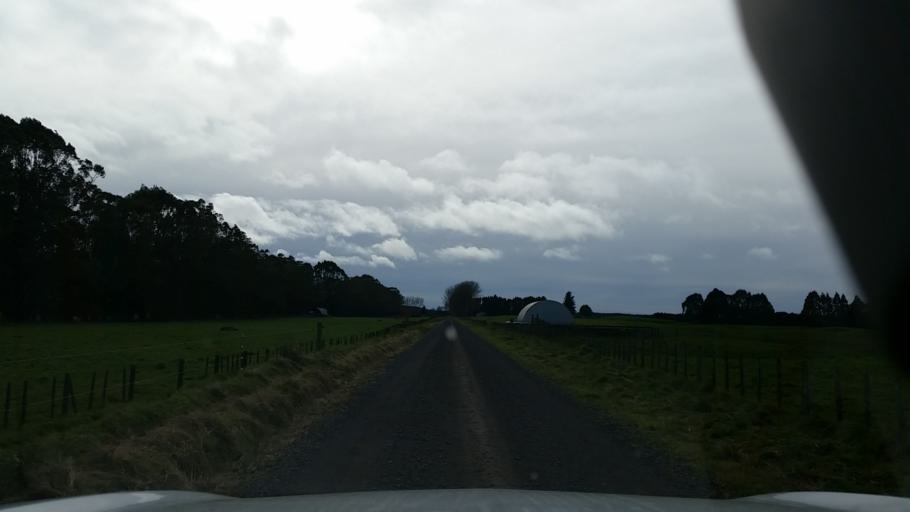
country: NZ
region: Bay of Plenty
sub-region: Whakatane District
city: Murupara
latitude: -38.4789
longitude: 176.4147
